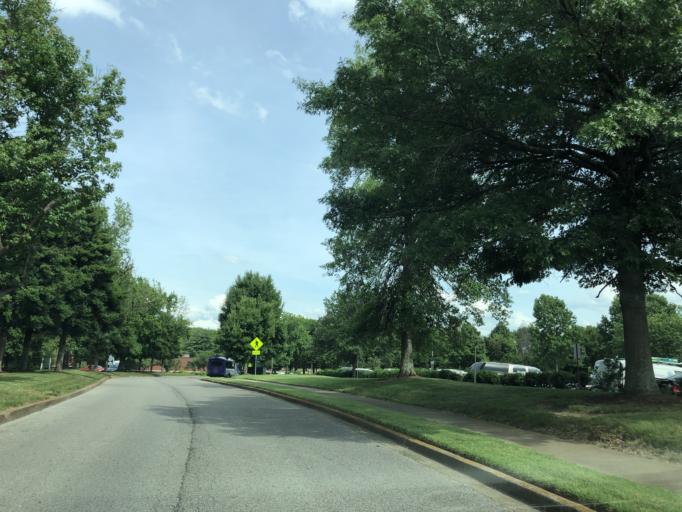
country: US
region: Tennessee
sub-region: Davidson County
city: Oak Hill
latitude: 36.0889
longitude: -86.7496
